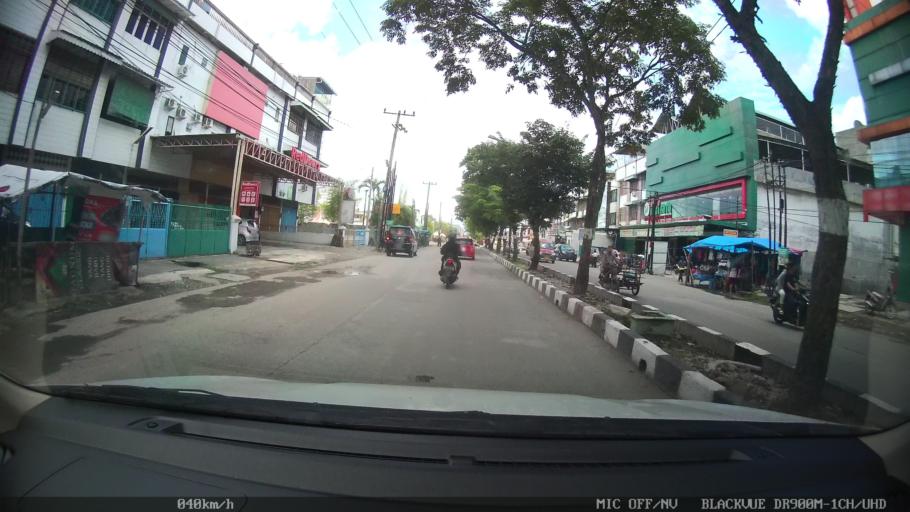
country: ID
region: North Sumatra
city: Medan
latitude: 3.5963
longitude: 98.7064
